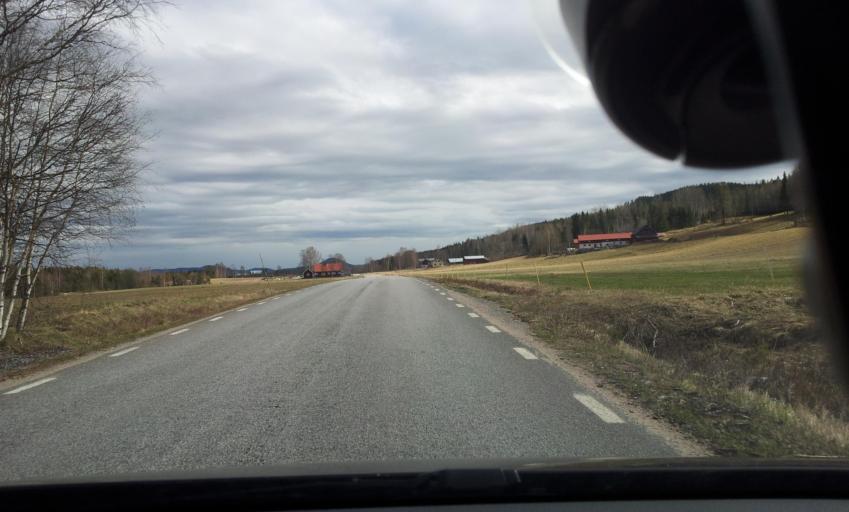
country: SE
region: Gaevleborg
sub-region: Ljusdals Kommun
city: Ljusdal
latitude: 61.7670
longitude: 16.0383
